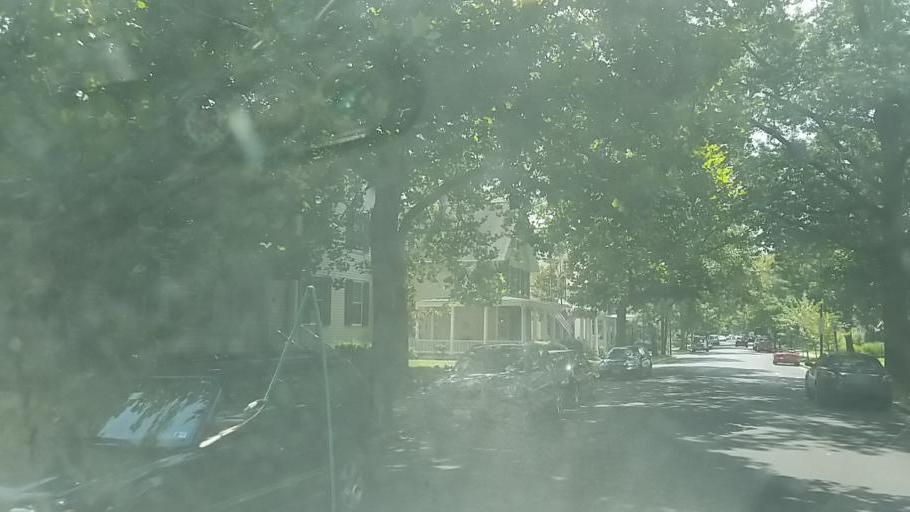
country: US
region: Maryland
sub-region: Talbot County
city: Easton
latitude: 38.7722
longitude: -76.0745
